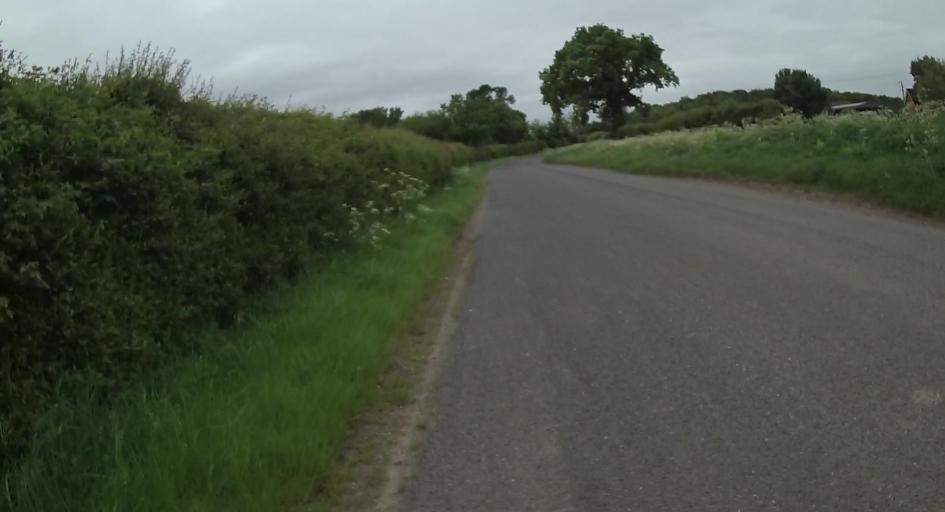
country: GB
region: England
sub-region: West Berkshire
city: Stratfield Mortimer
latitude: 51.3611
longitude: -1.0407
